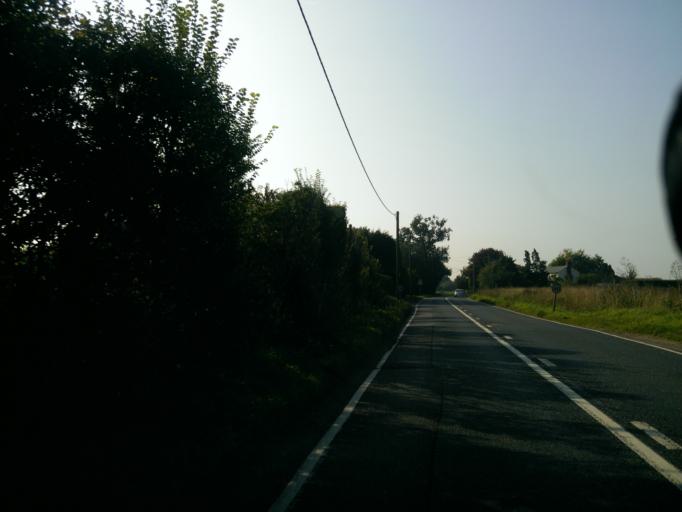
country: GB
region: England
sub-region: Essex
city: Layer de la Haye
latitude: 51.8561
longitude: 0.8189
